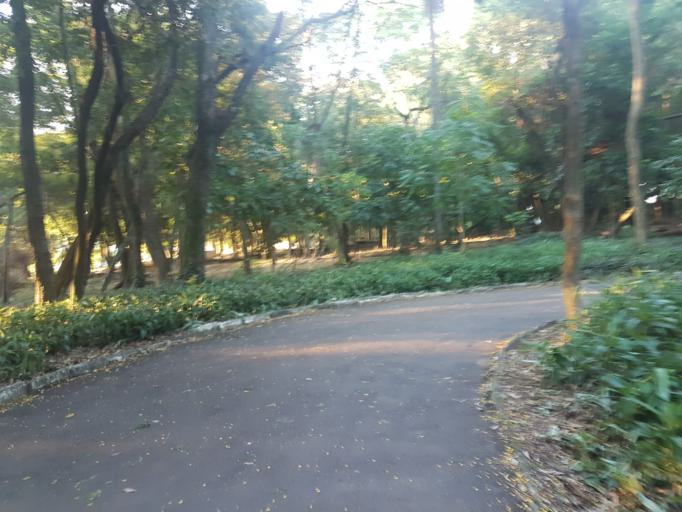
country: PY
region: Asuncion
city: Asuncion
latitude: -25.2761
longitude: -57.5820
